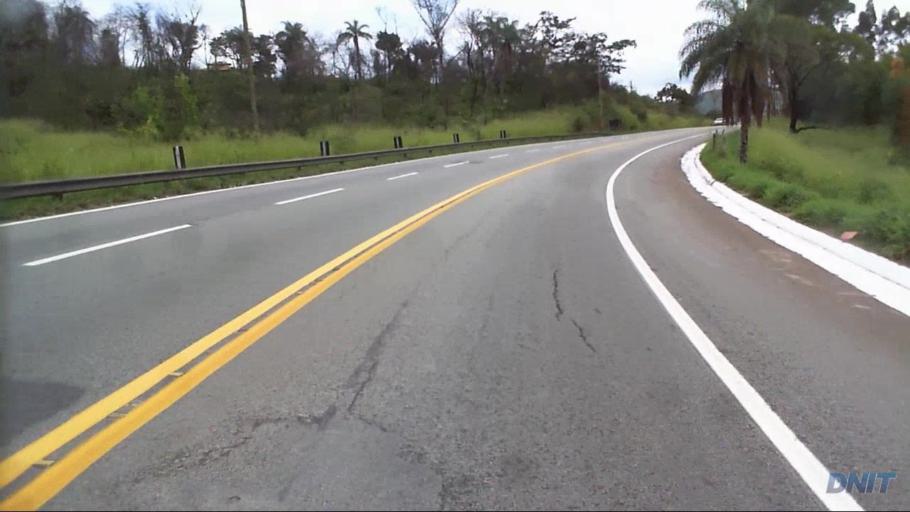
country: BR
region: Minas Gerais
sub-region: Caete
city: Caete
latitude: -19.7879
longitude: -43.7360
